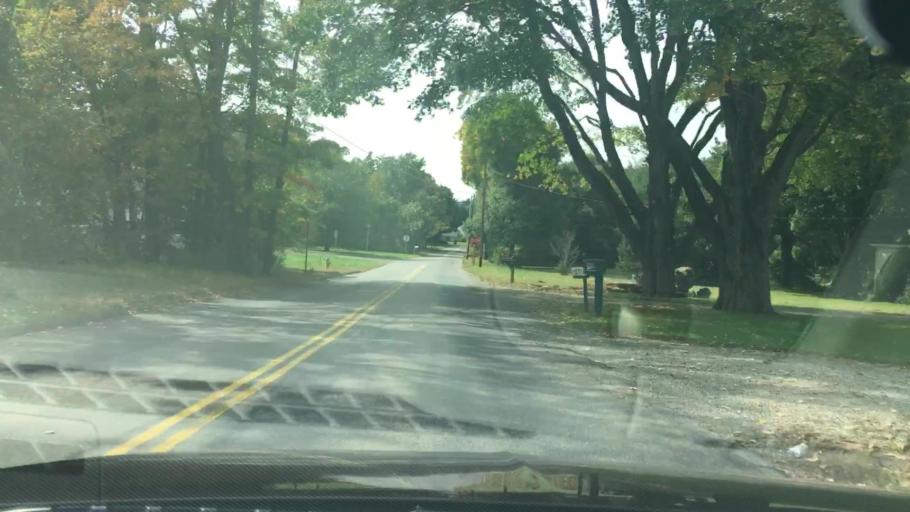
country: US
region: Connecticut
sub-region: Hartford County
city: Broad Brook
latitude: 41.8673
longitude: -72.5670
